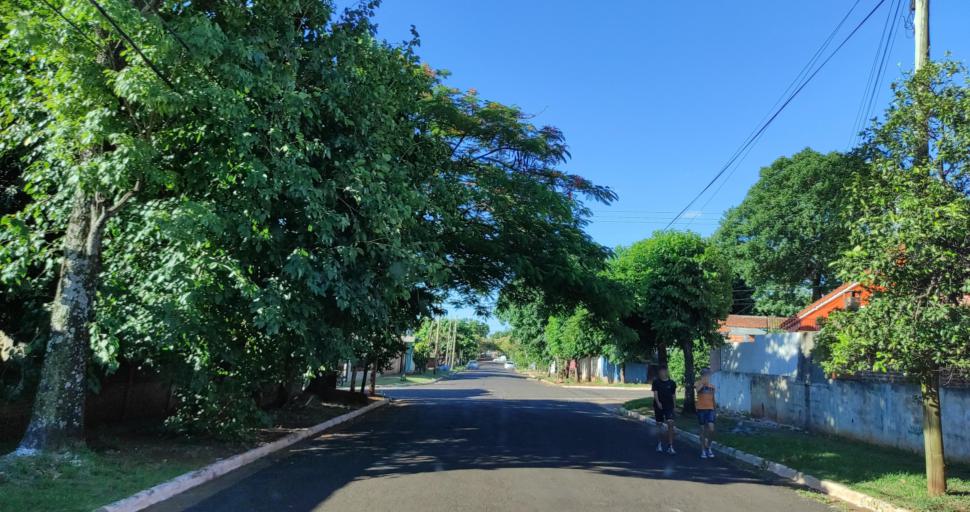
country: AR
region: Misiones
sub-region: Departamento de Capital
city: Posadas
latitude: -27.3762
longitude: -55.9311
